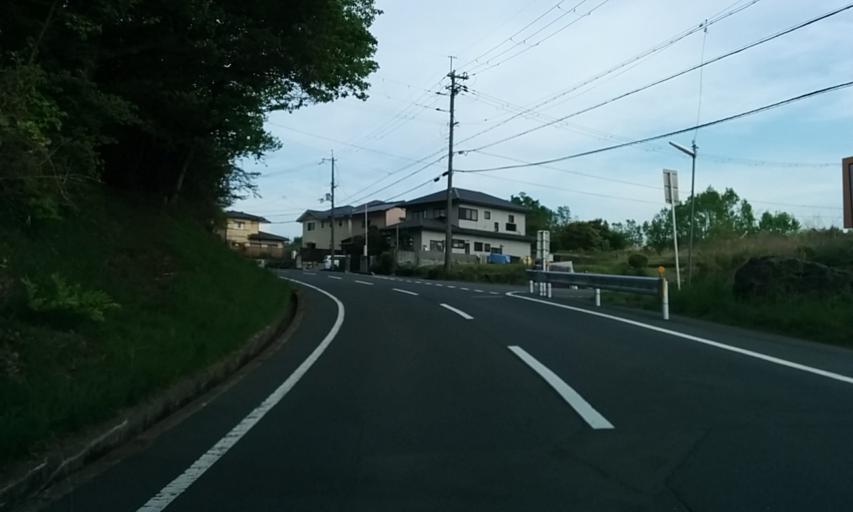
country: JP
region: Kyoto
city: Ayabe
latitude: 35.1752
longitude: 135.3773
